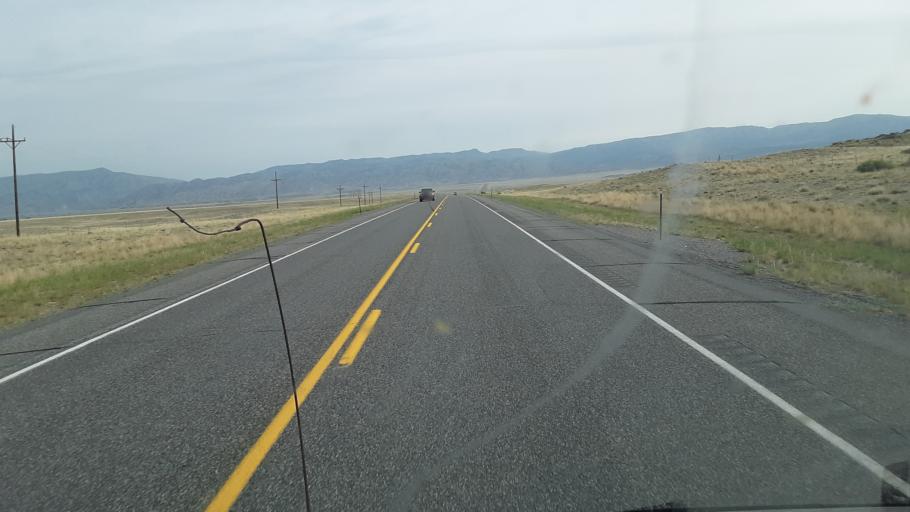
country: US
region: Wyoming
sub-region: Hot Springs County
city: Thermopolis
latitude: 43.3059
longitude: -108.1277
